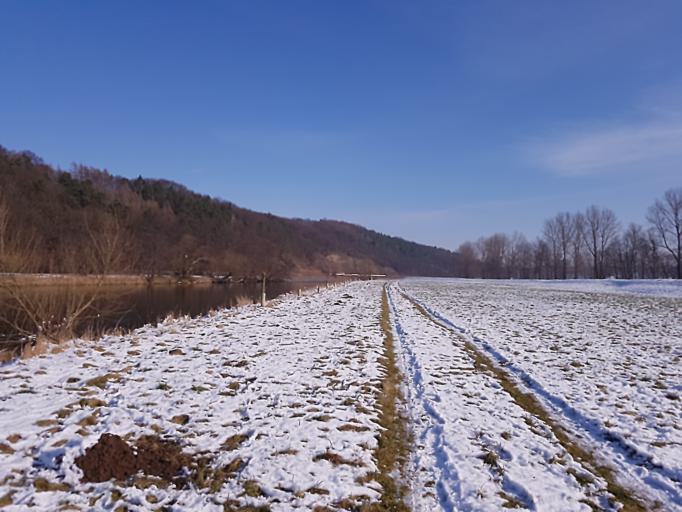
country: DE
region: Saxony
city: Leisnig
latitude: 51.1573
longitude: 12.9639
